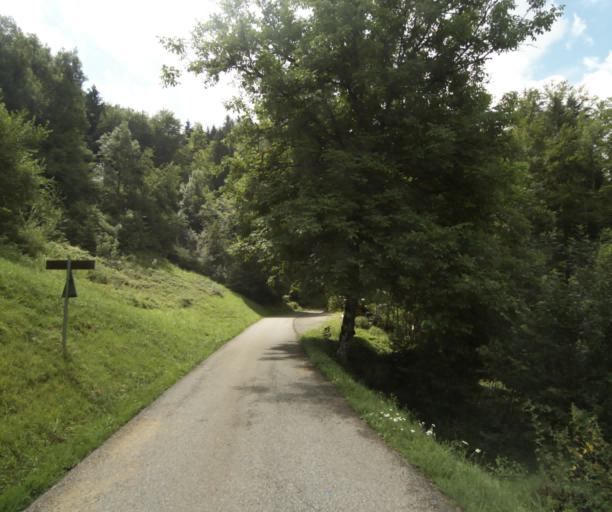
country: FR
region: Rhone-Alpes
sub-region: Departement de la Haute-Savoie
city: Thones
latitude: 45.8975
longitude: 6.3513
